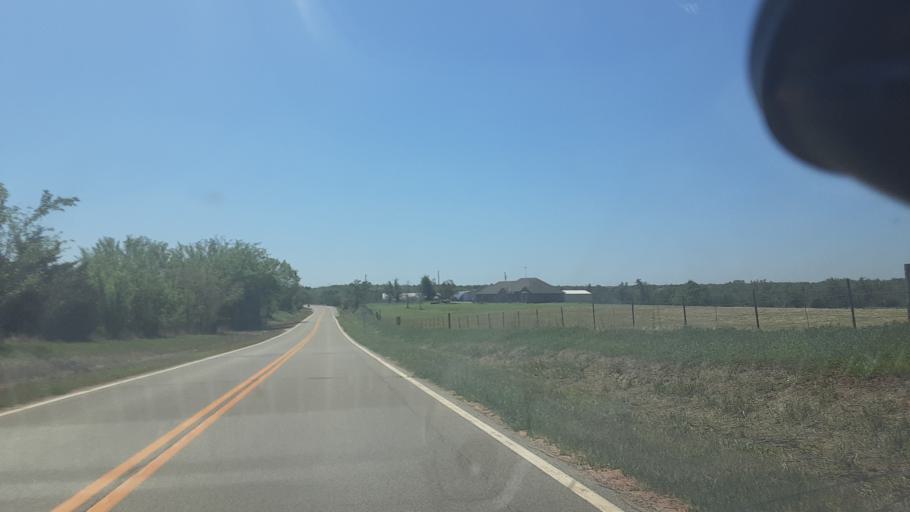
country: US
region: Oklahoma
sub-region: Logan County
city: Guthrie
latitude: 36.0568
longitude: -97.4077
